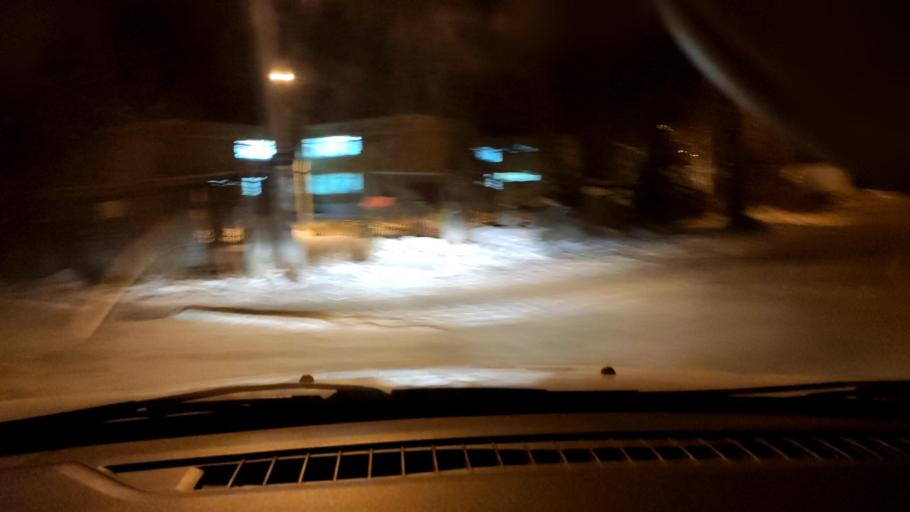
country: RU
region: Perm
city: Overyata
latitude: 58.0065
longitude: 55.9283
